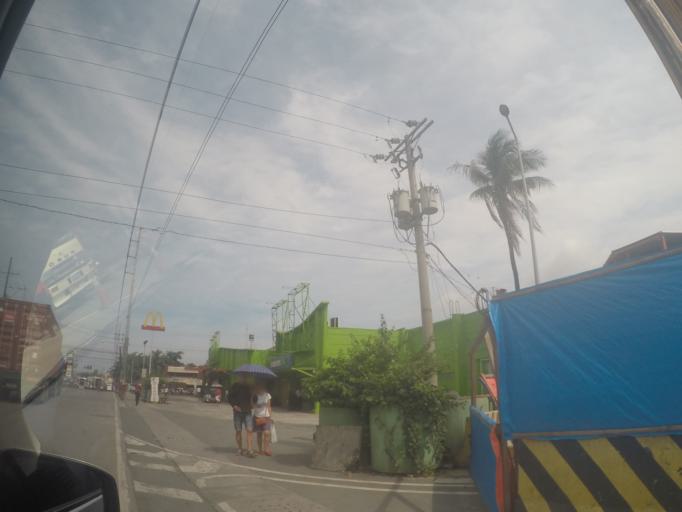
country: PH
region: Calabarzon
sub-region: Province of Rizal
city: Valenzuela
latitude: 14.6921
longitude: 120.9711
